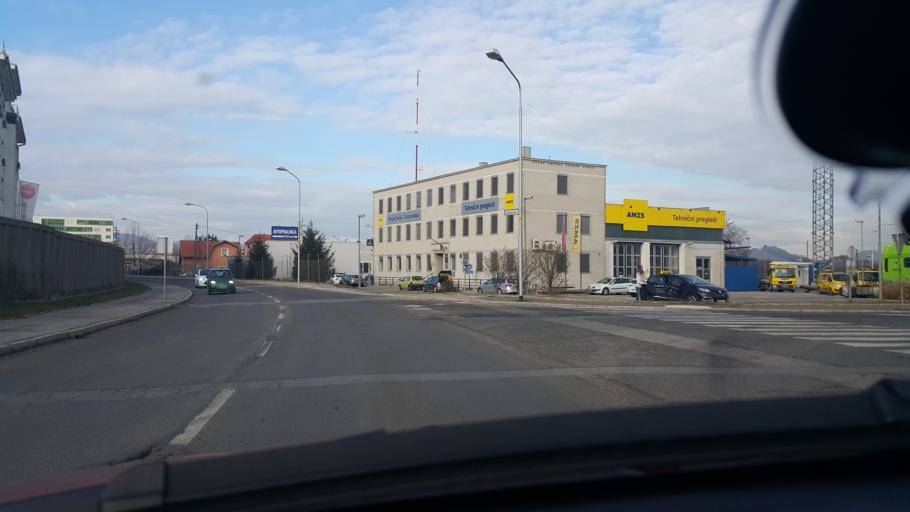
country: SI
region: Maribor
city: Maribor
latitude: 46.5369
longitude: 15.6546
